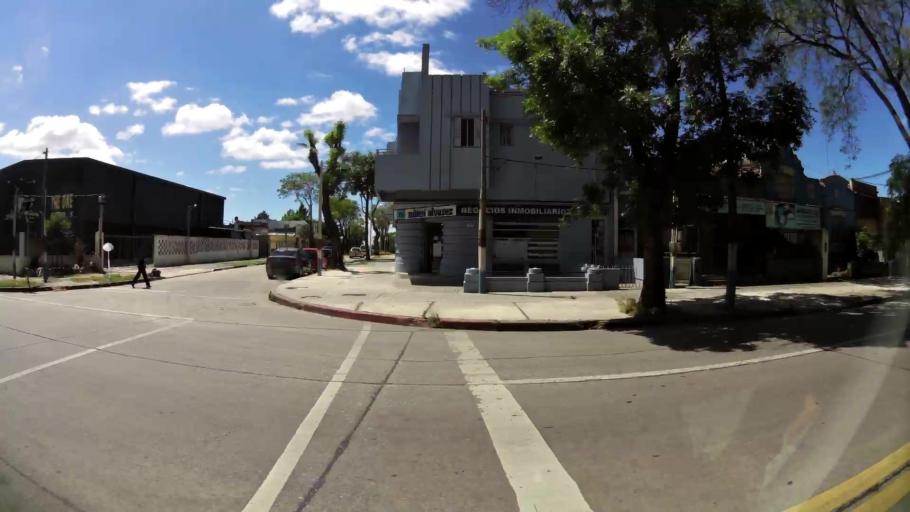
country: UY
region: Montevideo
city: Montevideo
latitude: -34.8546
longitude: -56.1311
